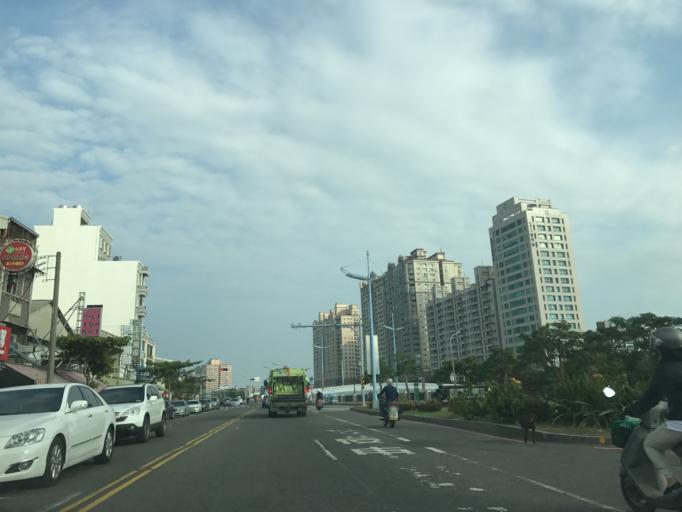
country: TW
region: Taiwan
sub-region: Tainan
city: Tainan
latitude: 22.9990
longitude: 120.1682
